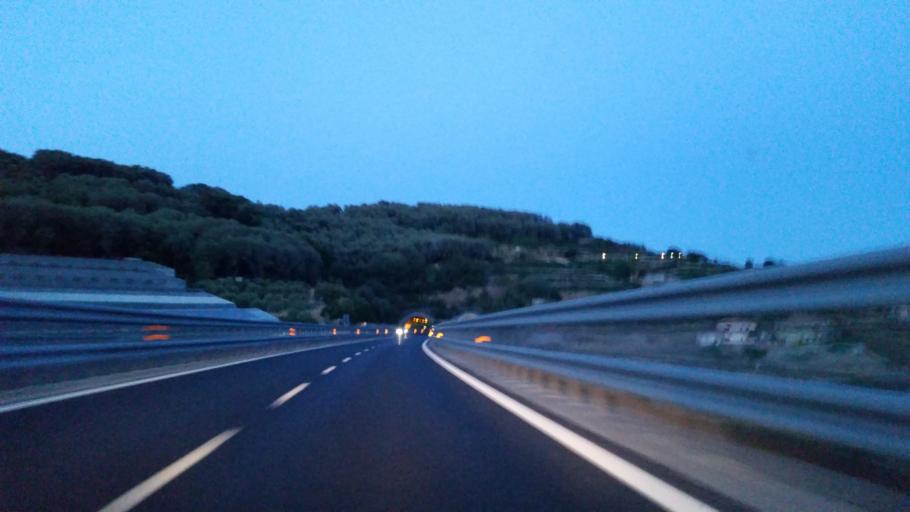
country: IT
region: Liguria
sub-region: Provincia di Imperia
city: San Lorenzo al Mare
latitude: 43.8628
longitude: 7.9565
